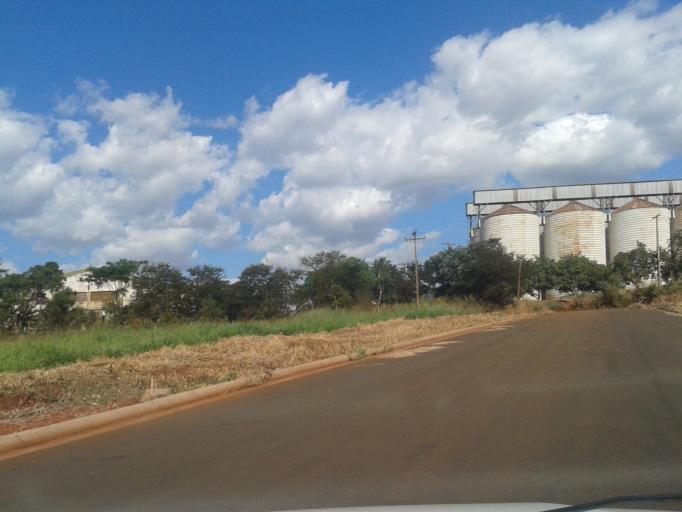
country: BR
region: Minas Gerais
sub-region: Capinopolis
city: Capinopolis
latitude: -18.6941
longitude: -49.5694
